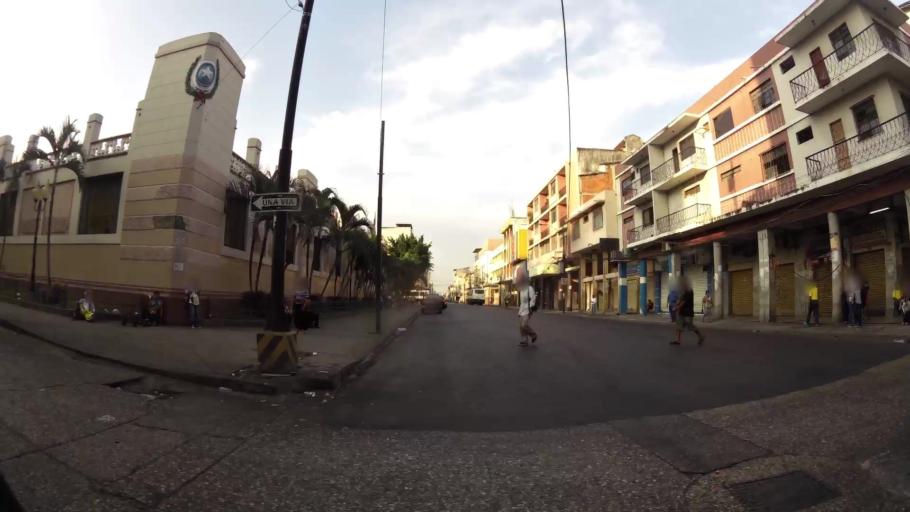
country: EC
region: Guayas
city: Guayaquil
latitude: -2.1933
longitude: -79.8881
